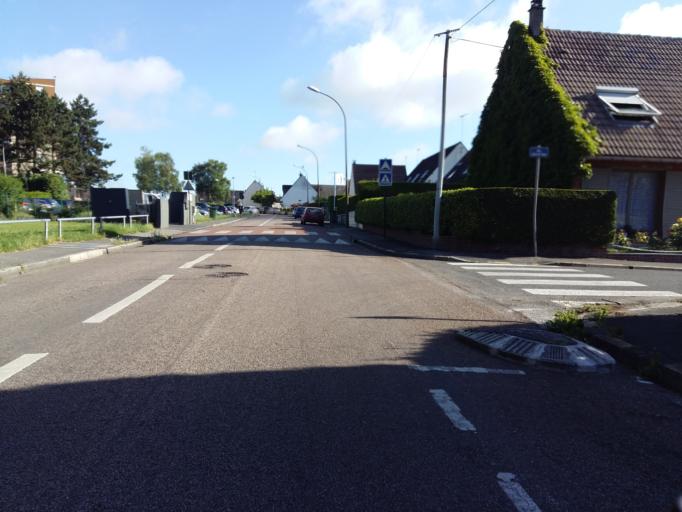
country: FR
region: Picardie
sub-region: Departement de la Somme
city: Rivery
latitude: 49.9123
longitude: 2.3267
